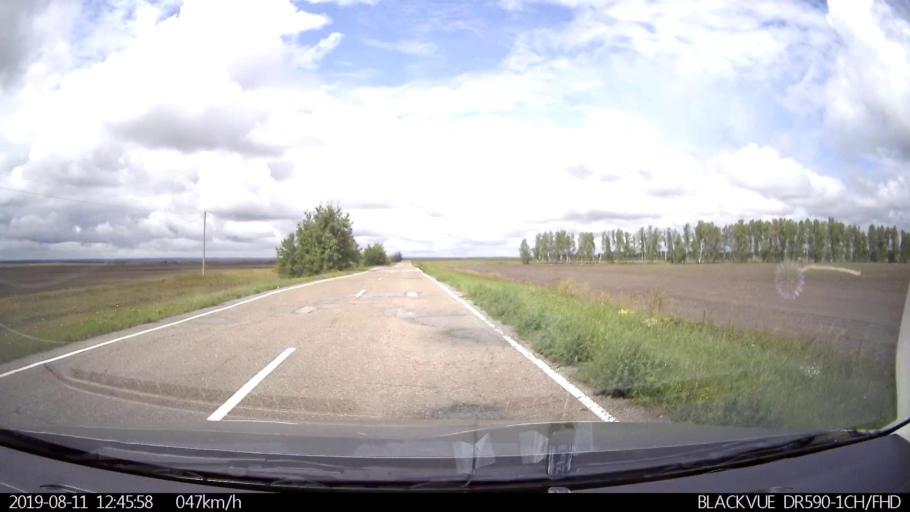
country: RU
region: Ulyanovsk
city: Ignatovka
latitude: 53.8620
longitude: 47.7231
